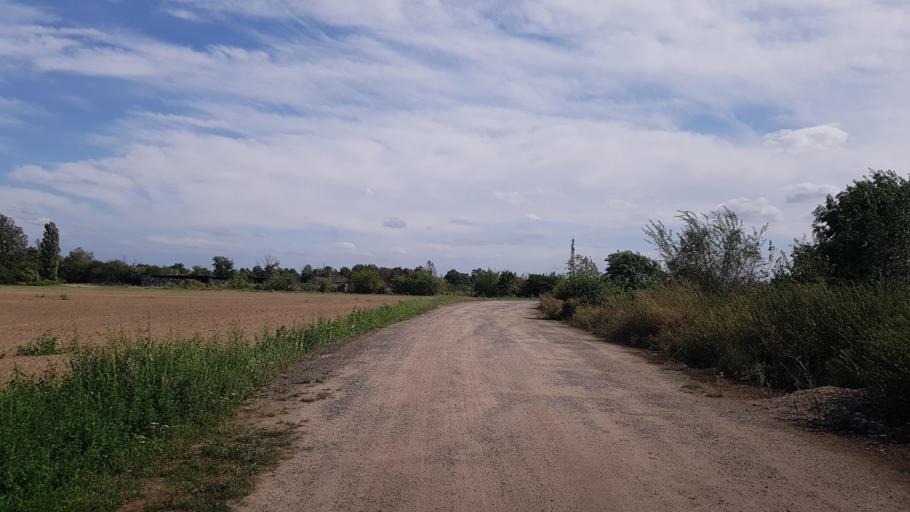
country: DE
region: Brandenburg
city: Muhlberg
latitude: 51.4287
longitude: 13.2622
